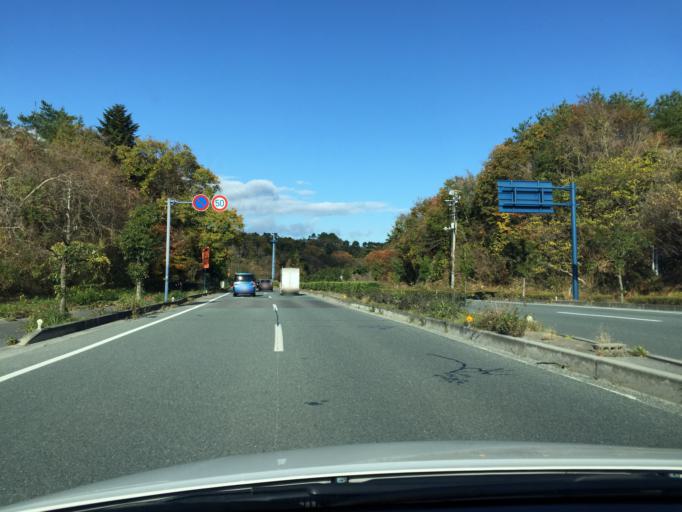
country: JP
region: Fukushima
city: Iwaki
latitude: 37.2445
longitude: 140.9996
